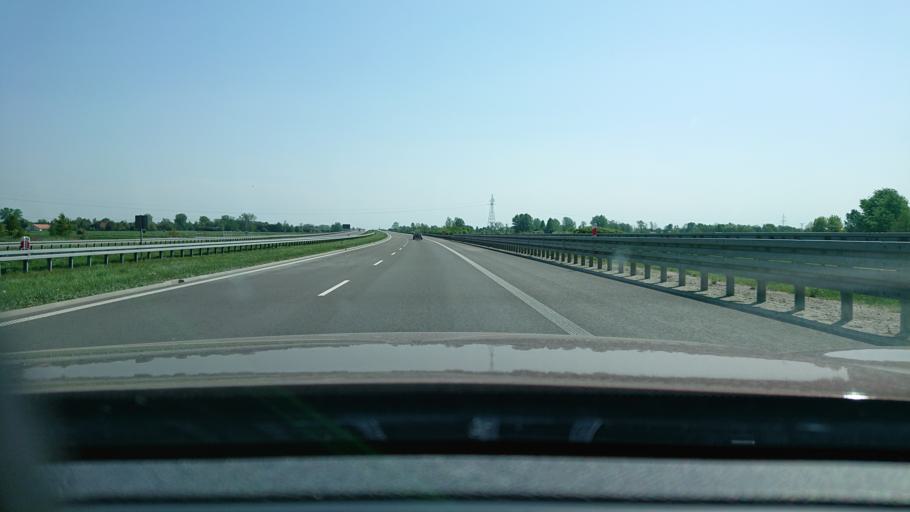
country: PL
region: Subcarpathian Voivodeship
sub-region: Powiat lancucki
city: Lancut
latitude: 50.0984
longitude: 22.2416
